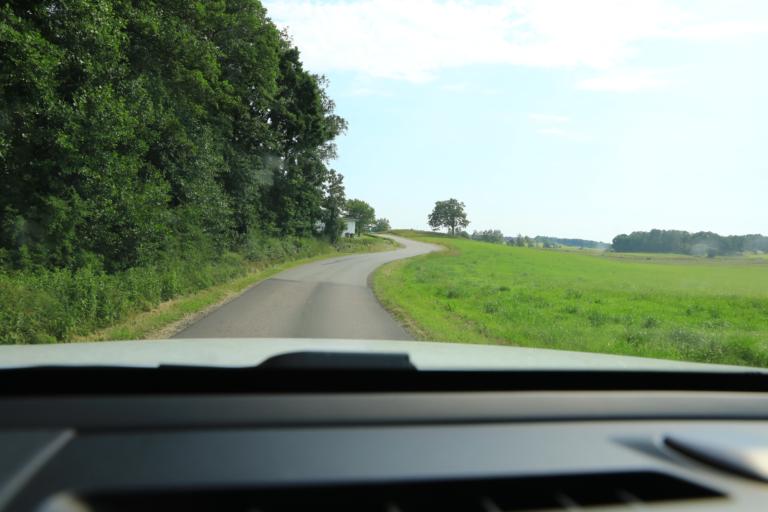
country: SE
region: Halland
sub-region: Varbergs Kommun
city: Varberg
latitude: 57.1480
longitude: 12.3217
